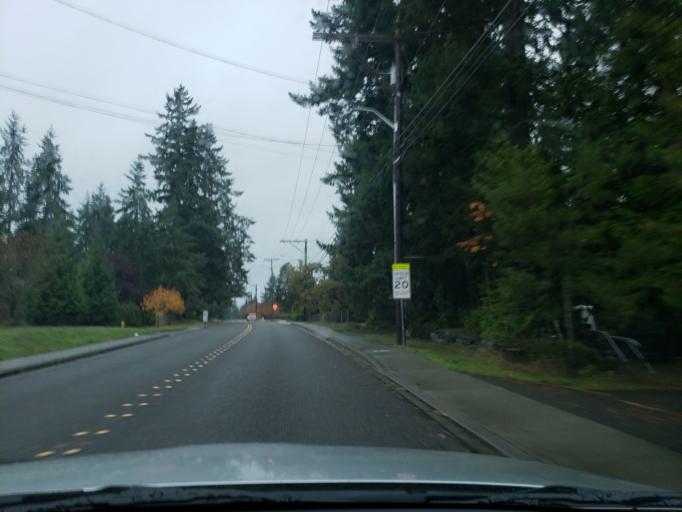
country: US
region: Washington
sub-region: Snohomish County
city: Lynnwood
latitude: 47.8393
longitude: -122.3182
